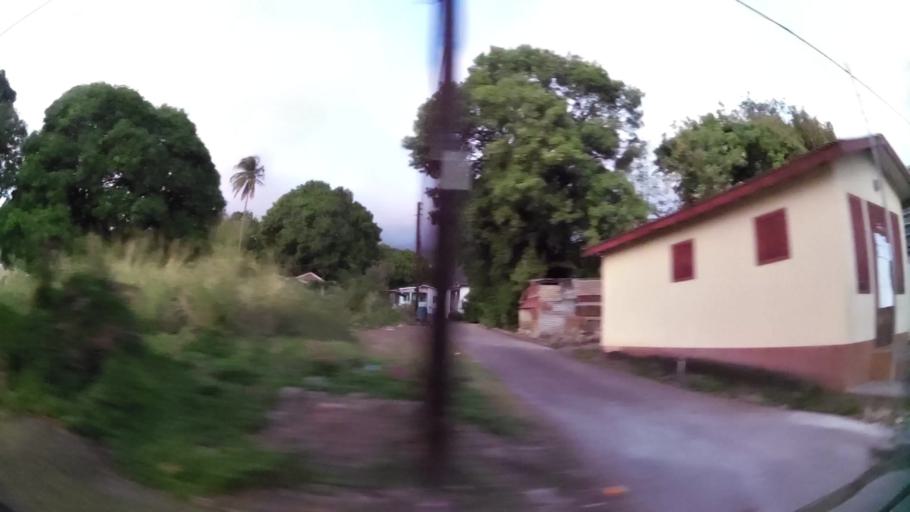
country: KN
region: Saint Thomas Middle Island
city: Middle Island
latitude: 17.3267
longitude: -62.8138
